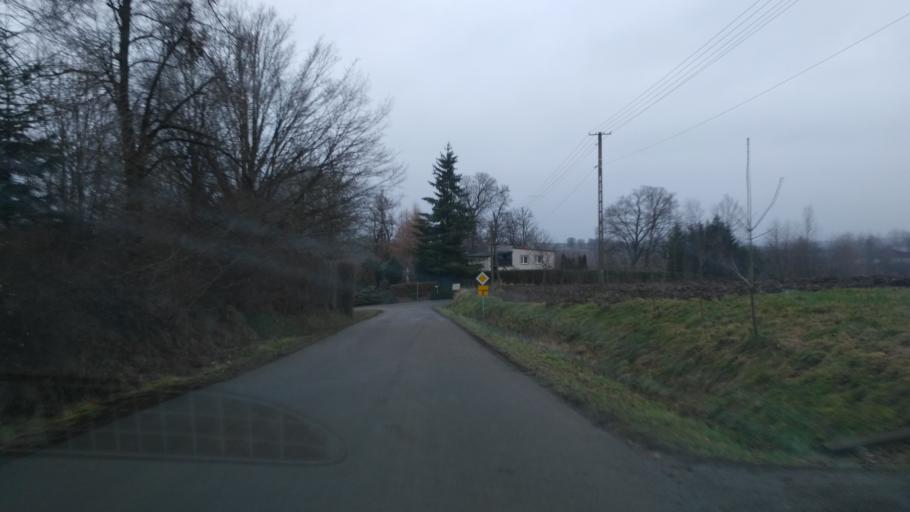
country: PL
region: Subcarpathian Voivodeship
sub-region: Powiat jaroslawski
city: Pruchnik
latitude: 49.9310
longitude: 22.5355
